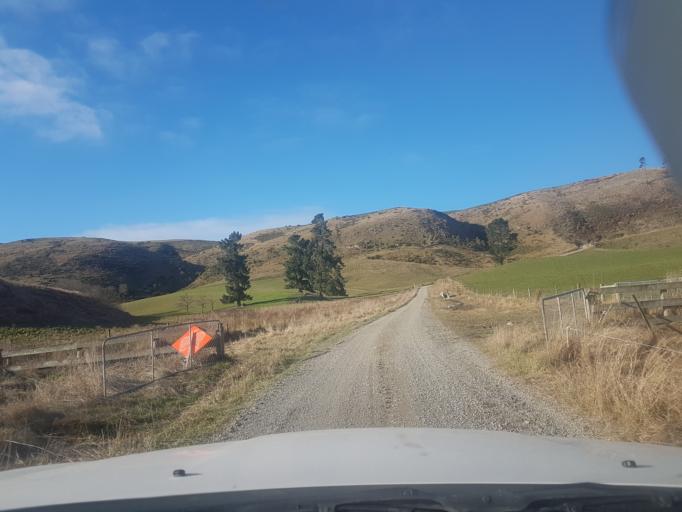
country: NZ
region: Canterbury
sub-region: Timaru District
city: Pleasant Point
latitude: -44.1653
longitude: 170.8750
